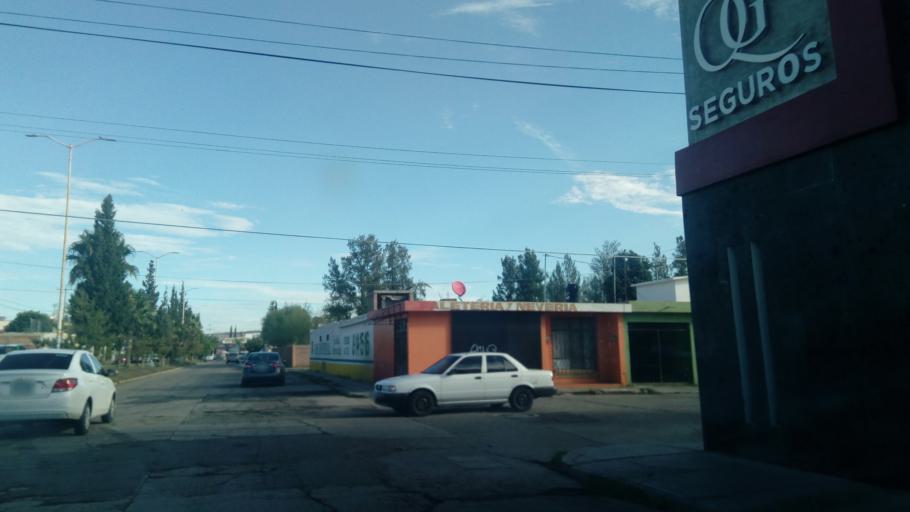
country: MX
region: Durango
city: Victoria de Durango
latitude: 24.0540
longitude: -104.6084
